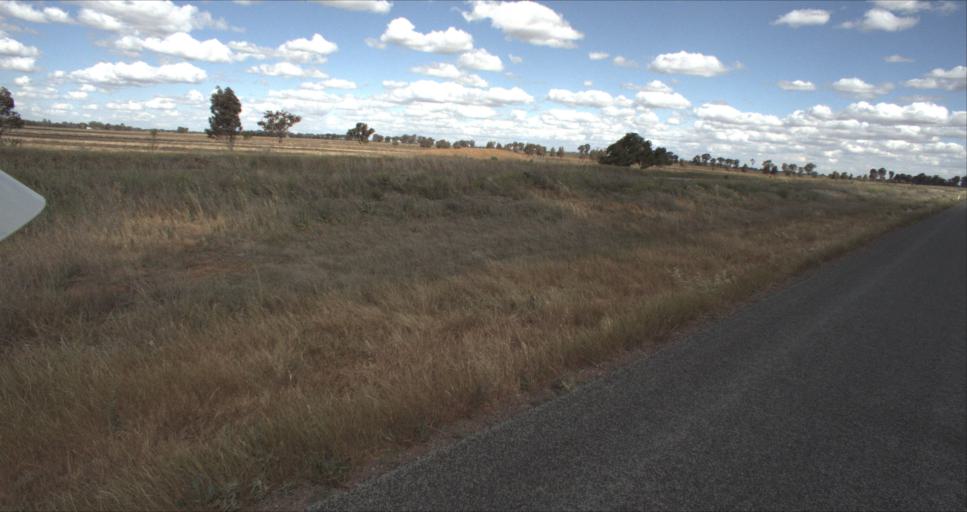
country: AU
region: New South Wales
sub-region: Leeton
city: Leeton
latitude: -34.4516
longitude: 146.2545
